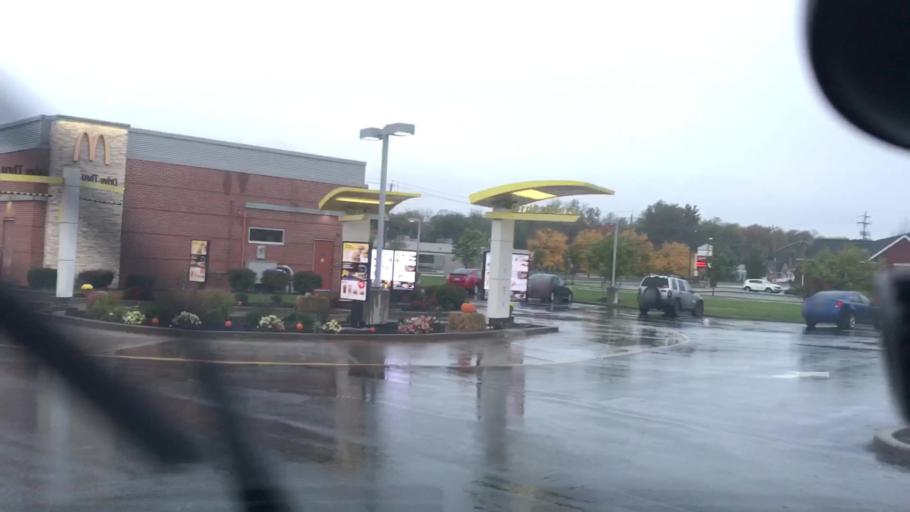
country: US
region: New York
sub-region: Erie County
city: Depew
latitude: 42.8834
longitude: -78.6958
